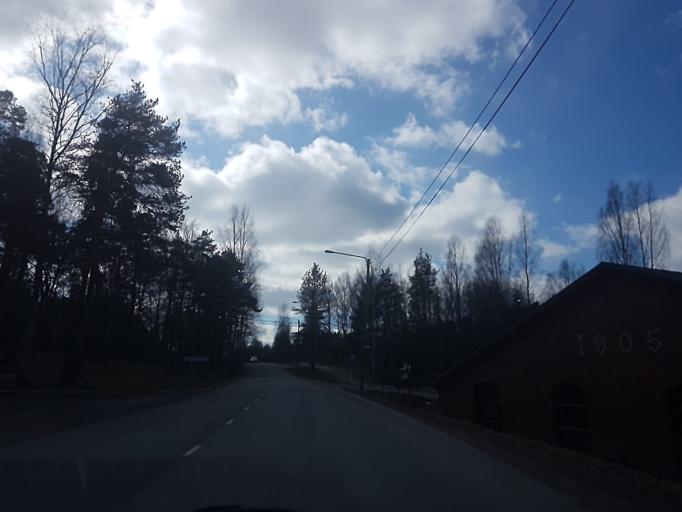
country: FI
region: Uusimaa
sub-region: Porvoo
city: Porvoo
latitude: 60.3956
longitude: 25.6488
